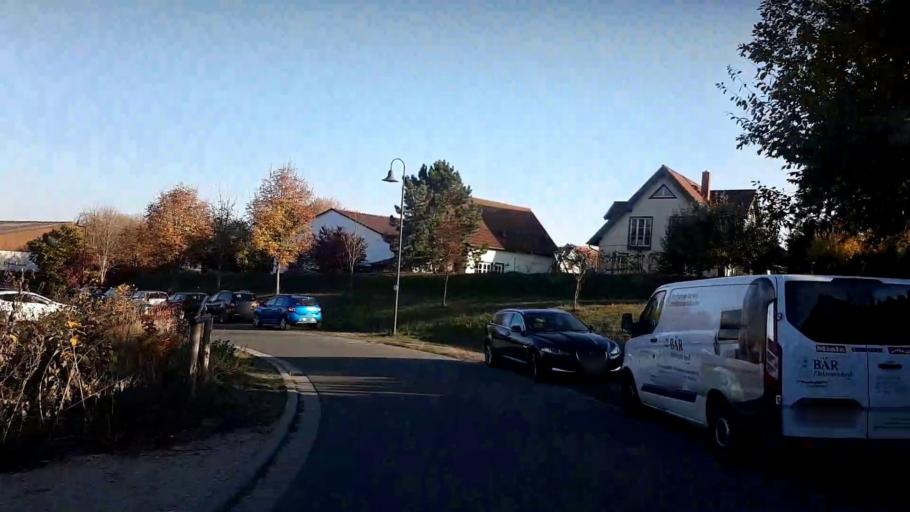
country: DE
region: Bavaria
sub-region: Upper Franconia
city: Walsdorf
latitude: 49.8734
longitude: 10.7922
